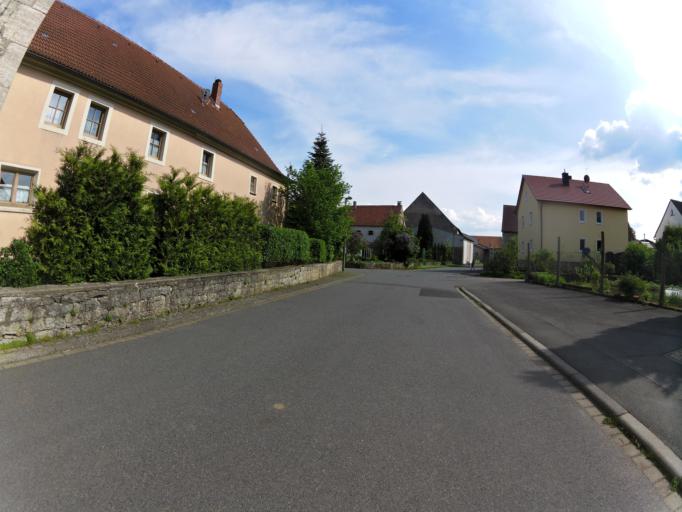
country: DE
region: Bavaria
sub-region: Regierungsbezirk Unterfranken
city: Giebelstadt
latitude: 49.6124
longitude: 9.9479
